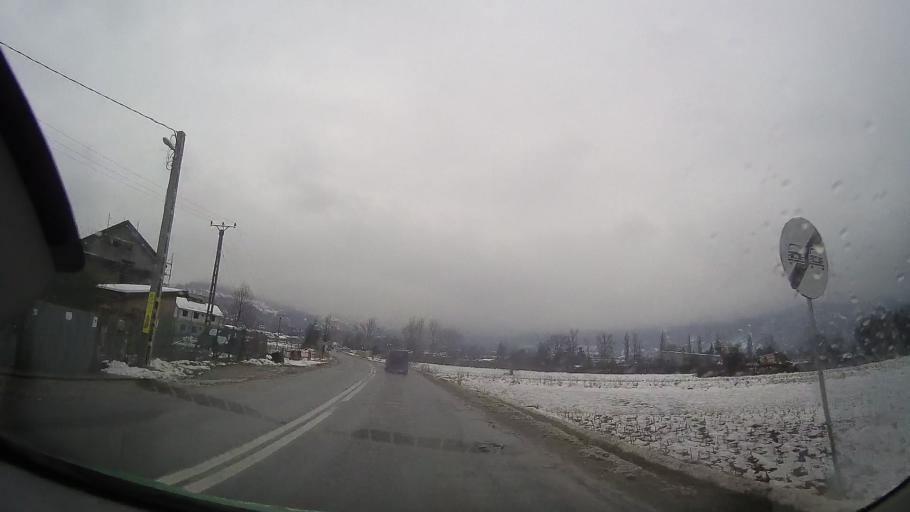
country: RO
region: Neamt
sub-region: Comuna Pangarati
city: Stejaru
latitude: 46.9230
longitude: 26.1898
